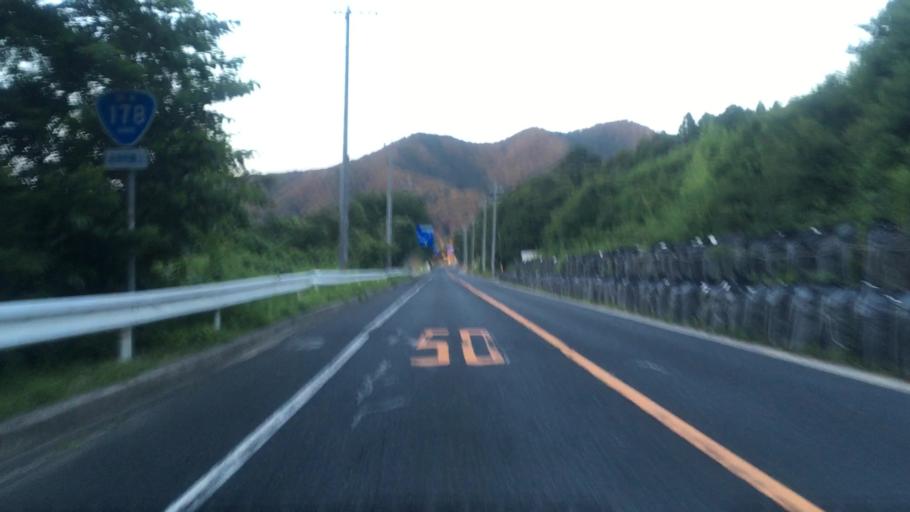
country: JP
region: Tottori
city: Tottori
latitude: 35.5960
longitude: 134.3627
